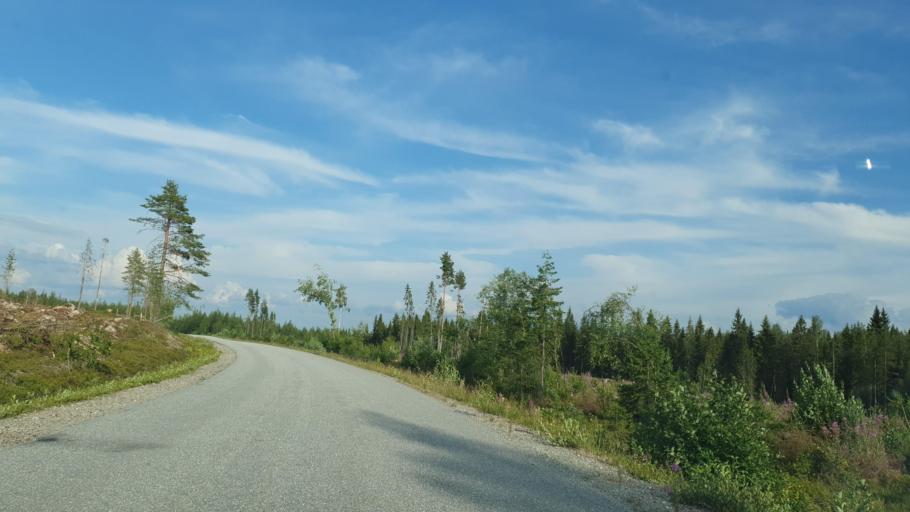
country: FI
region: Kainuu
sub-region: Kehys-Kainuu
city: Kuhmo
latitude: 64.3152
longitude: 29.5024
